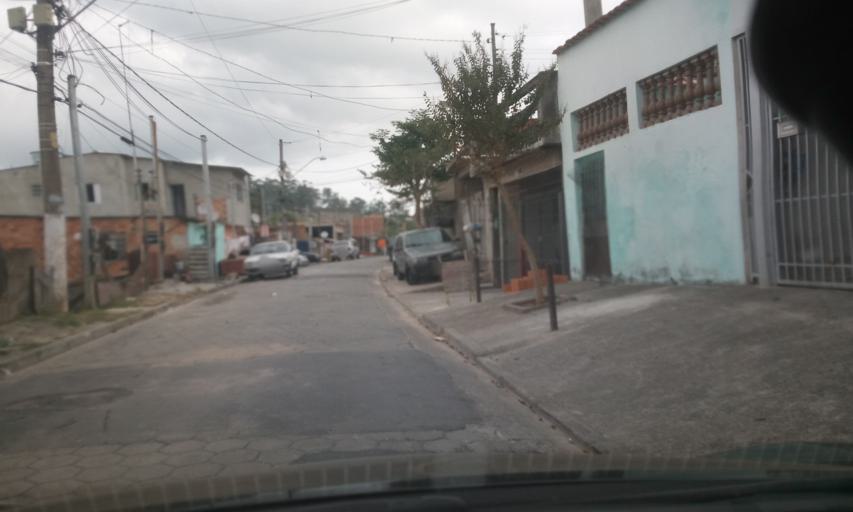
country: BR
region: Sao Paulo
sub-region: Diadema
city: Diadema
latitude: -23.7706
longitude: -46.6093
